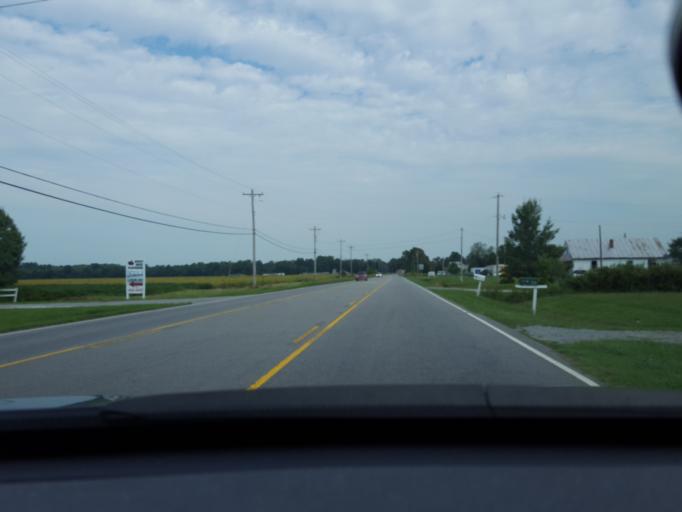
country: US
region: North Carolina
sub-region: Chowan County
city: Edenton
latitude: 36.0907
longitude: -76.6294
